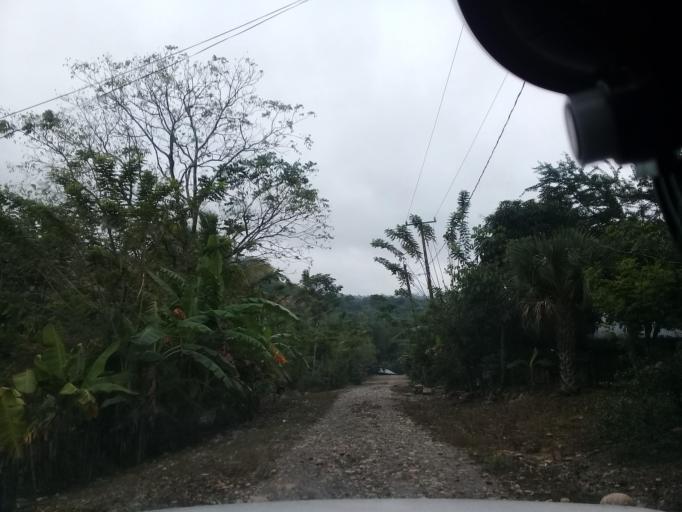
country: MX
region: Veracruz
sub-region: Chalma
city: San Pedro Coyutla
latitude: 21.2260
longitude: -98.4312
